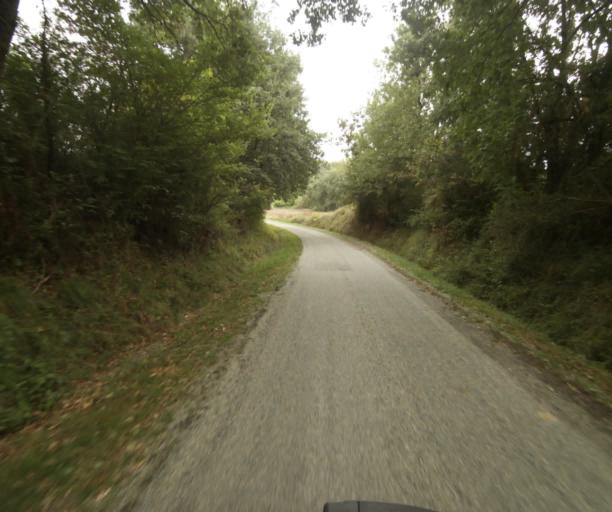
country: FR
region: Midi-Pyrenees
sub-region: Departement du Tarn-et-Garonne
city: Verdun-sur-Garonne
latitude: 43.8488
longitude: 1.1143
